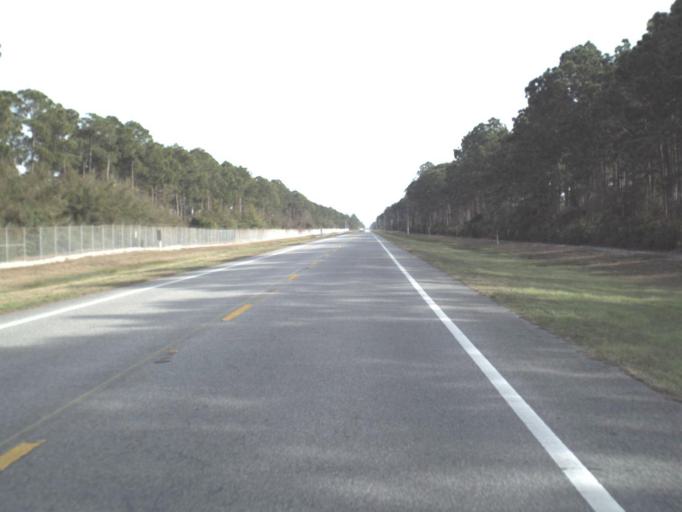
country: US
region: Florida
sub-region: Bay County
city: Tyndall Air Force Base
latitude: 30.0577
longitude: -85.5743
